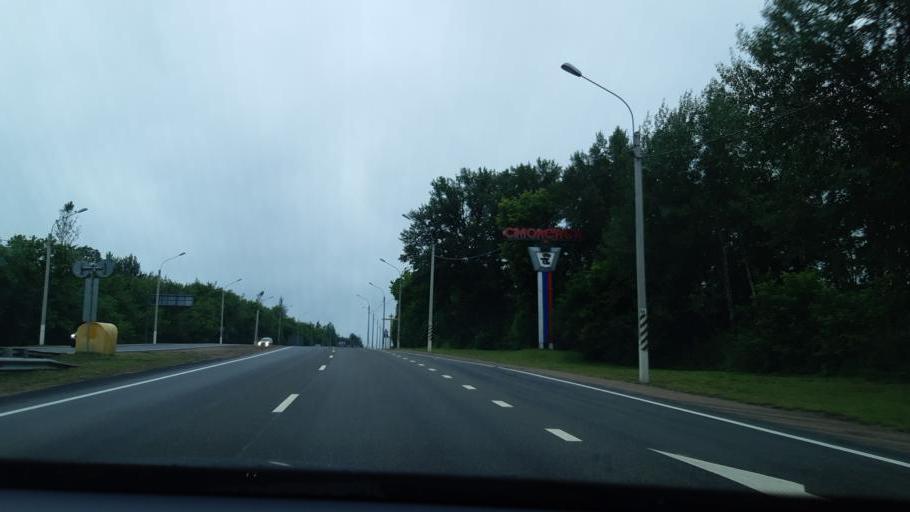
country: RU
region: Smolensk
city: Talashkino
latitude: 54.7108
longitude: 32.1132
